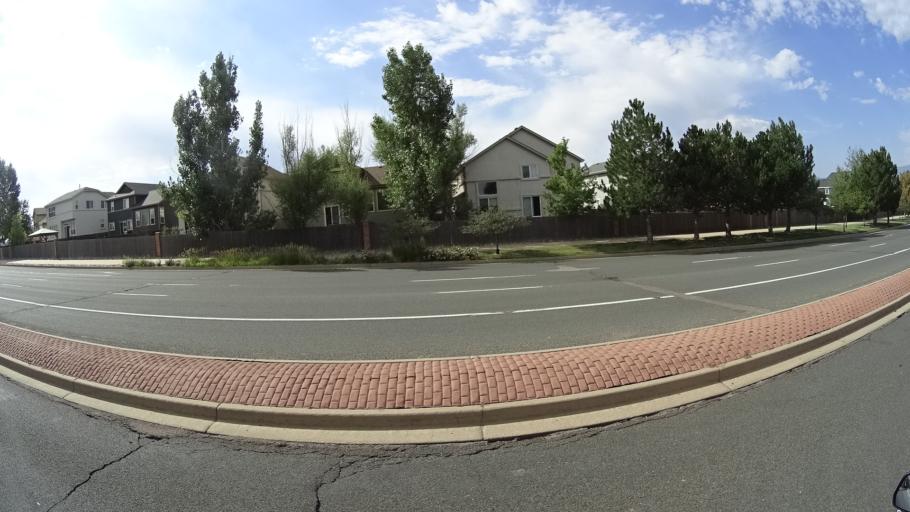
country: US
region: Colorado
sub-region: El Paso County
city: Cimarron Hills
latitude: 38.9125
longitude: -104.6966
